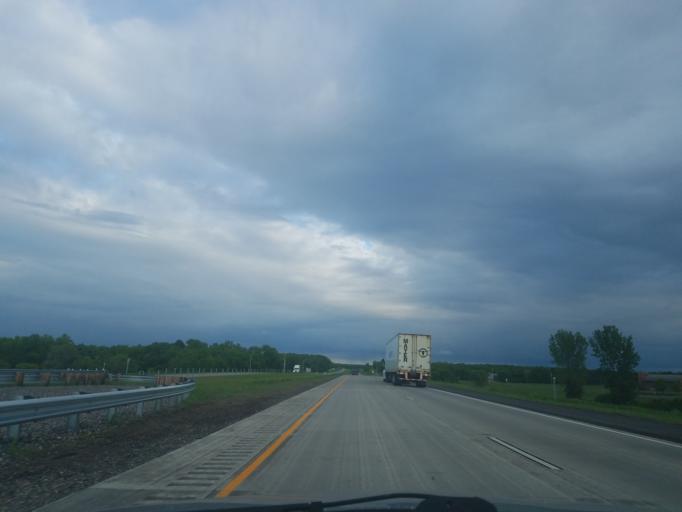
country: US
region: Minnesota
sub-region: Stearns County
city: Saint Joseph
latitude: 45.5578
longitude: -94.3395
